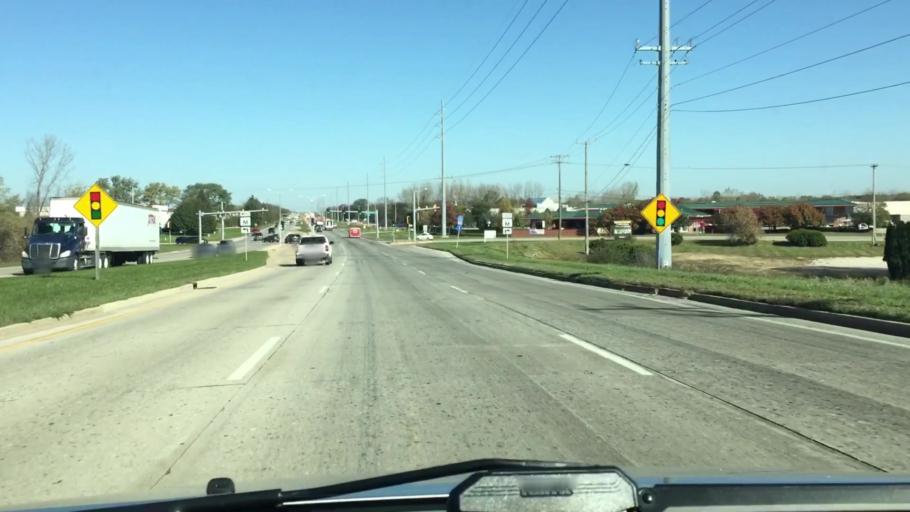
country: US
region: Wisconsin
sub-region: Waukesha County
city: Waukesha
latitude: 43.0571
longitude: -88.2057
